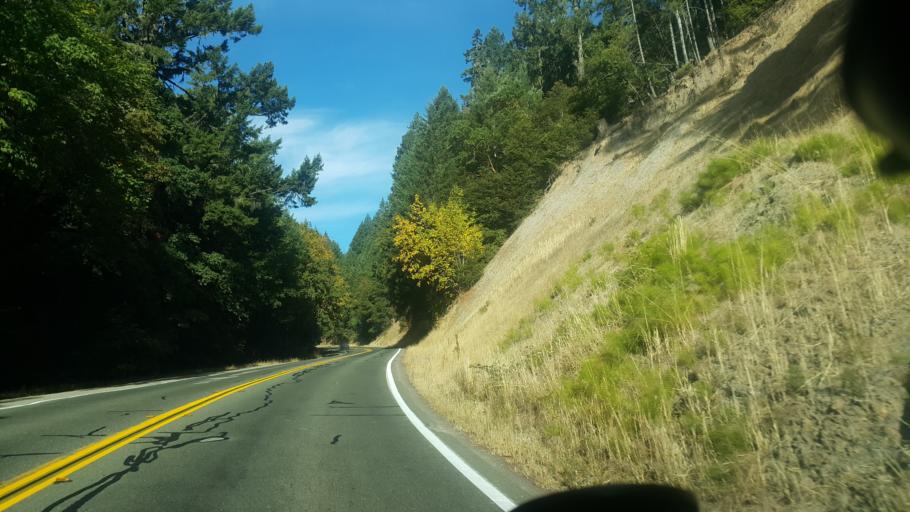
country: US
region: California
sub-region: Mendocino County
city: Brooktrails
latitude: 39.3875
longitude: -123.4364
